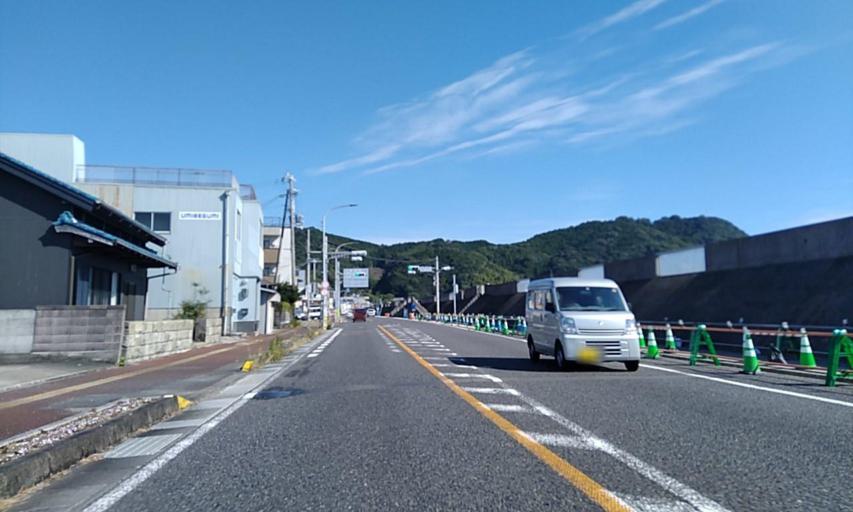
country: JP
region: Wakayama
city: Shingu
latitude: 33.8878
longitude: 136.1020
